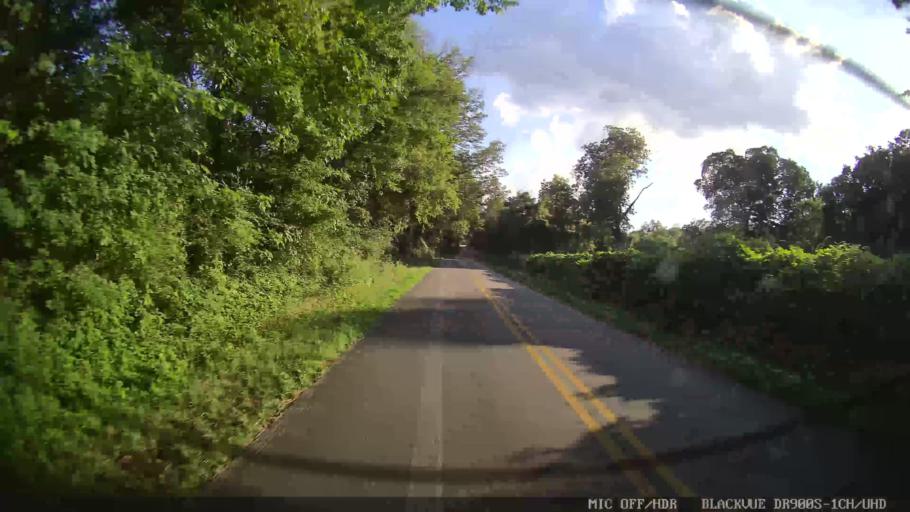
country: US
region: Georgia
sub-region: Bartow County
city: Rydal
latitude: 34.2902
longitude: -84.7418
